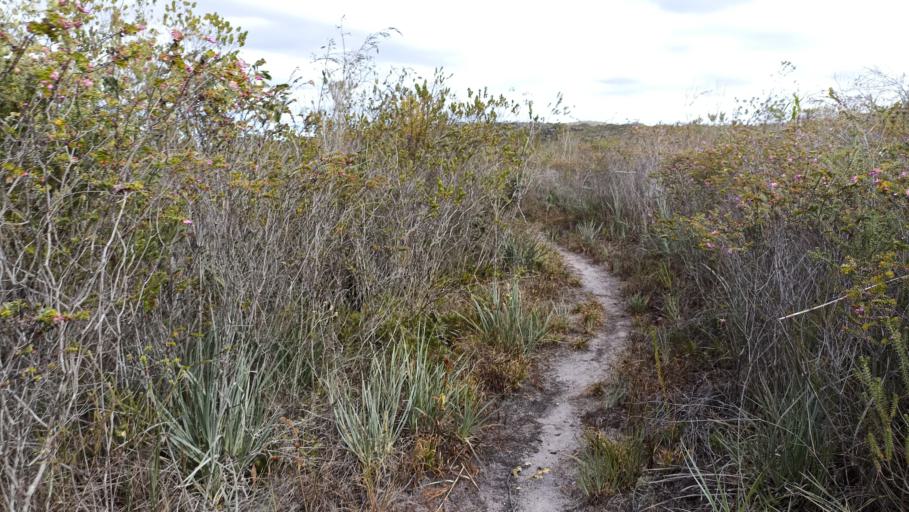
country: BR
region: Bahia
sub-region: Andarai
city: Vera Cruz
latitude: -12.9918
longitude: -41.3785
